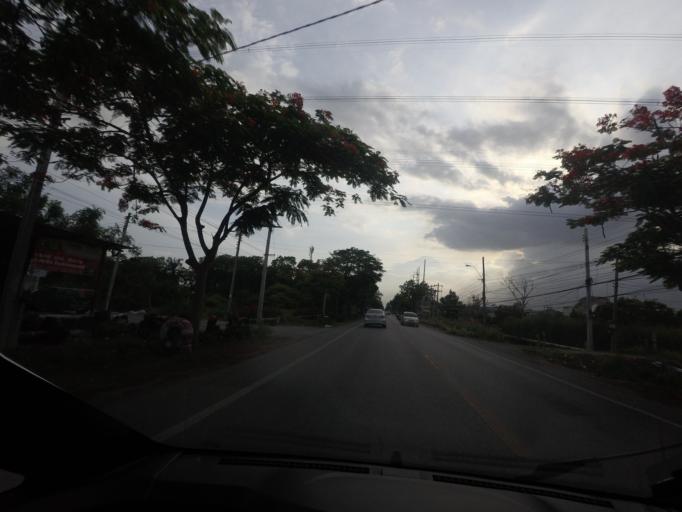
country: TH
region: Bangkok
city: Nong Chok
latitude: 13.8588
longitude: 100.8452
